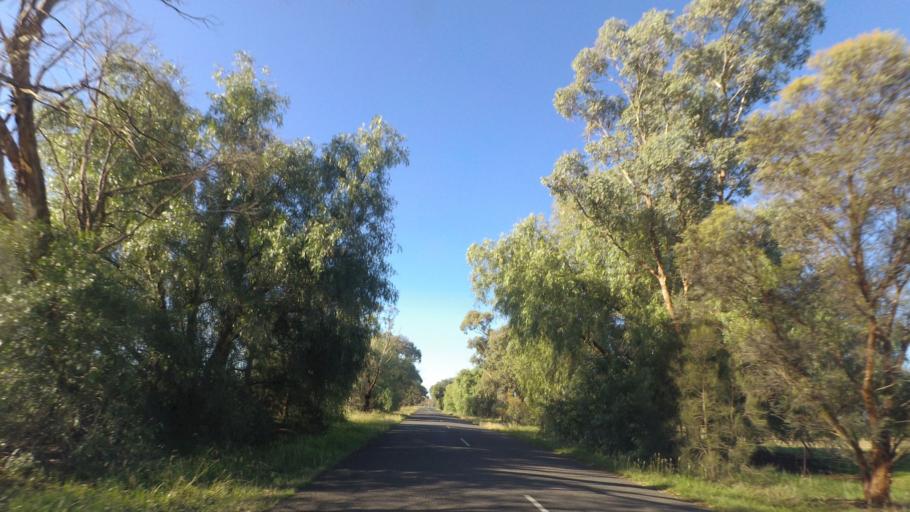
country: AU
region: Victoria
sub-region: Greater Bendigo
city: Epsom
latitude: -36.6479
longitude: 144.5293
